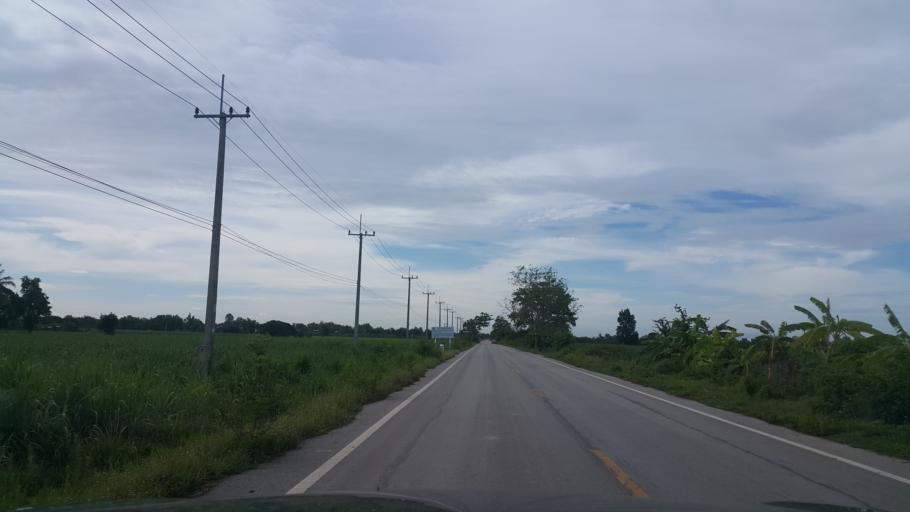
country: TH
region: Sukhothai
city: Si Nakhon
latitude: 17.2769
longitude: 99.9769
